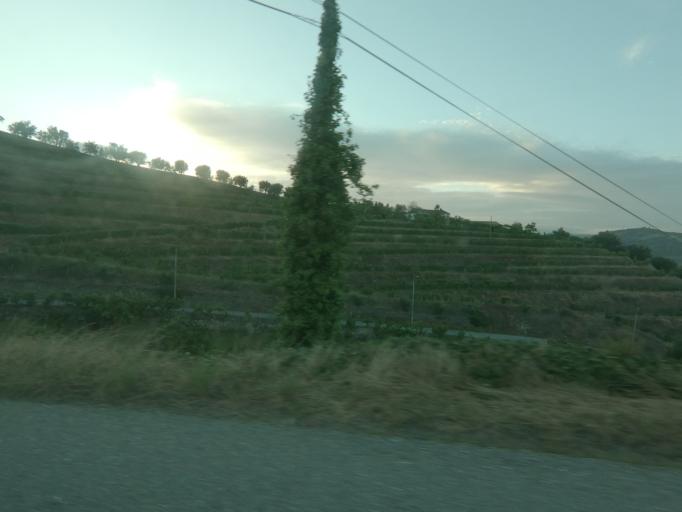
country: PT
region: Vila Real
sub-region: Peso da Regua
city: Peso da Regua
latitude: 41.1320
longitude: -7.7468
